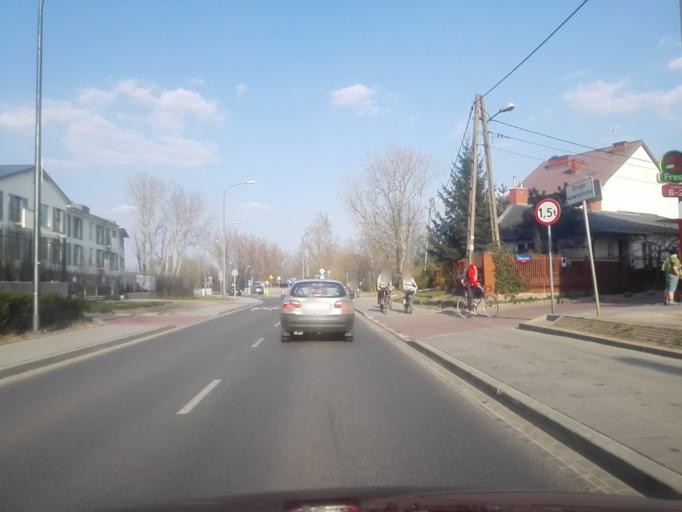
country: PL
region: Masovian Voivodeship
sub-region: Warszawa
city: Wilanow
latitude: 52.1603
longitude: 21.0911
